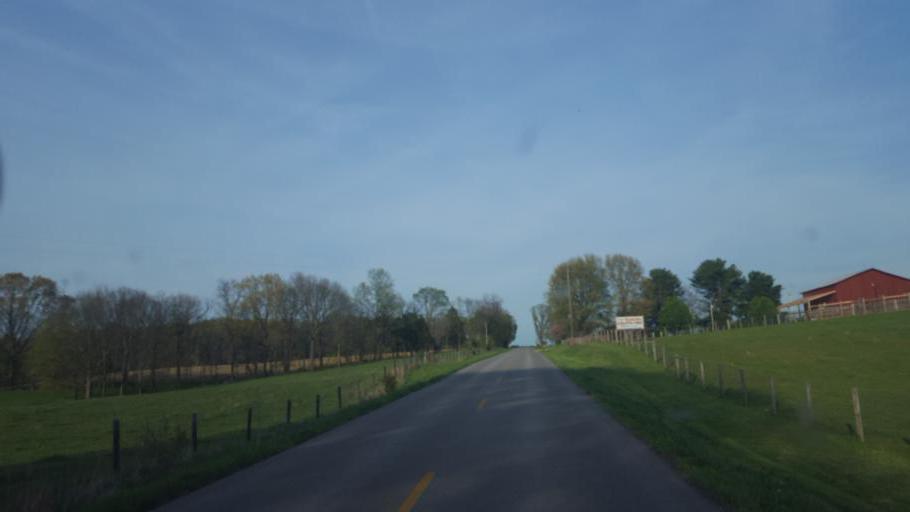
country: US
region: Kentucky
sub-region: Barren County
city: Glasgow
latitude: 36.9396
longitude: -86.0639
